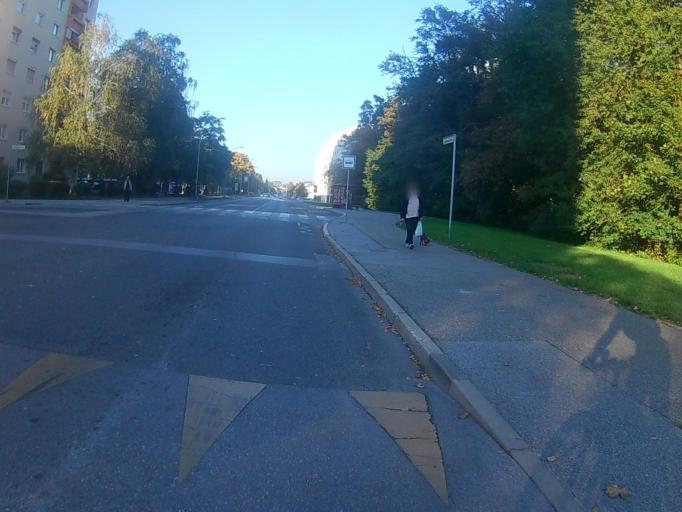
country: SI
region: Maribor
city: Maribor
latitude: 46.5369
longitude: 15.6377
